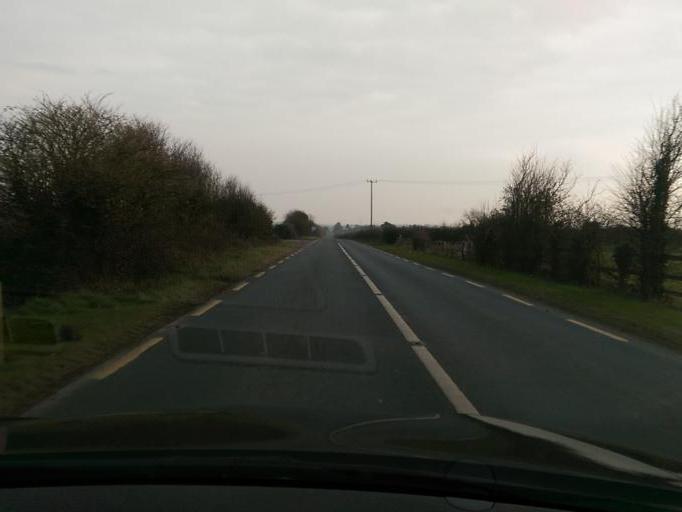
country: IE
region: Leinster
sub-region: An Iarmhi
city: Athlone
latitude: 53.4896
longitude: -7.8570
